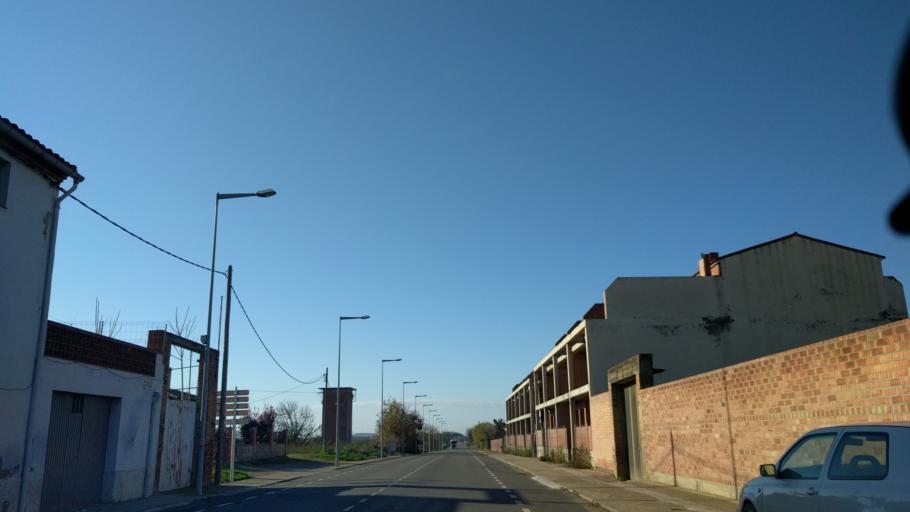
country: ES
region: Catalonia
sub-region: Provincia de Lleida
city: Corbins
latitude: 41.6872
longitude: 0.7259
